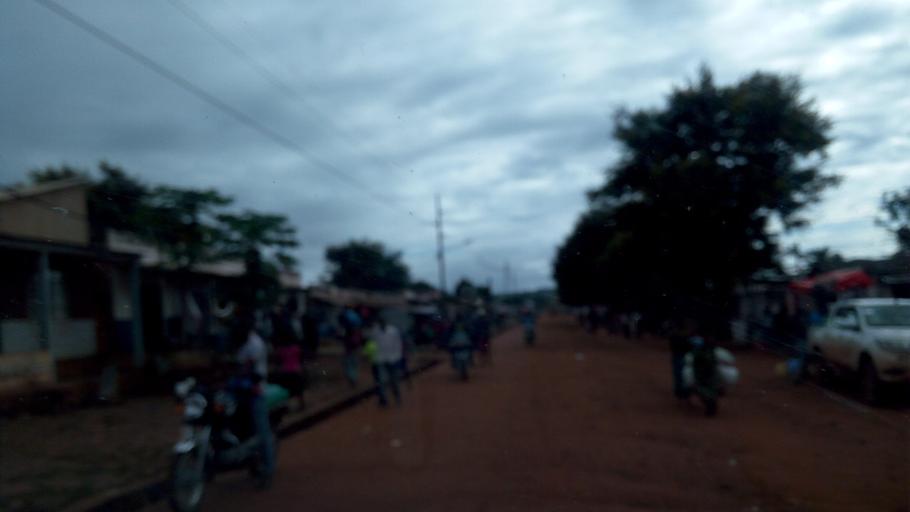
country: ZM
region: Northern
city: Kaputa
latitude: -8.4663
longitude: 28.8994
